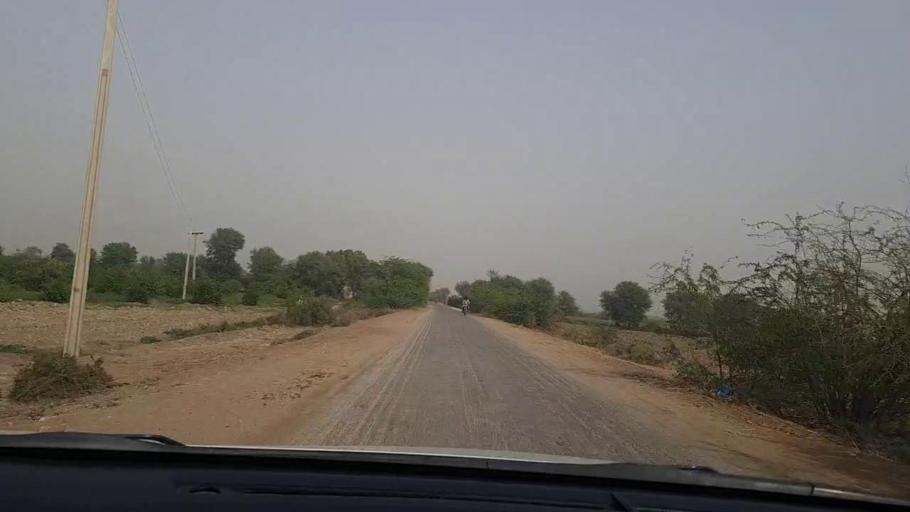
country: PK
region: Sindh
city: Samaro
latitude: 25.3823
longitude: 69.3402
